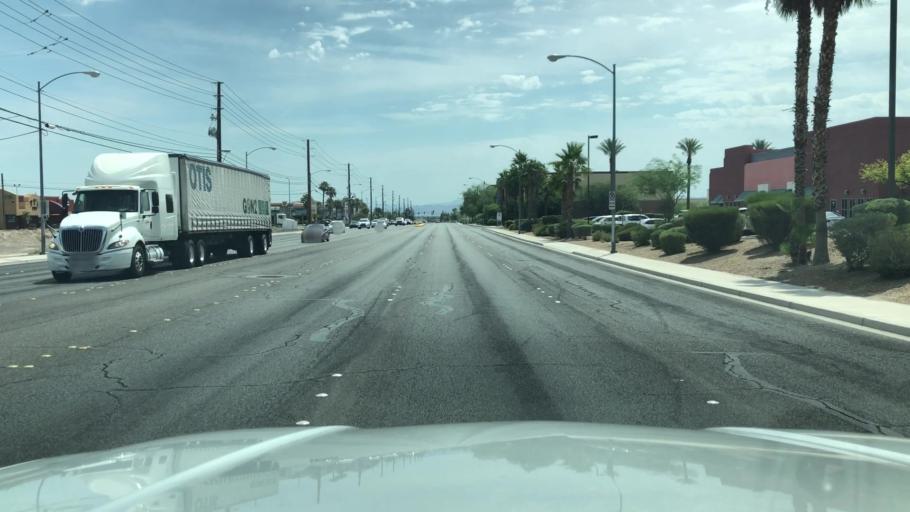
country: US
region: Nevada
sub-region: Clark County
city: Paradise
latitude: 36.0568
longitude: -115.1605
